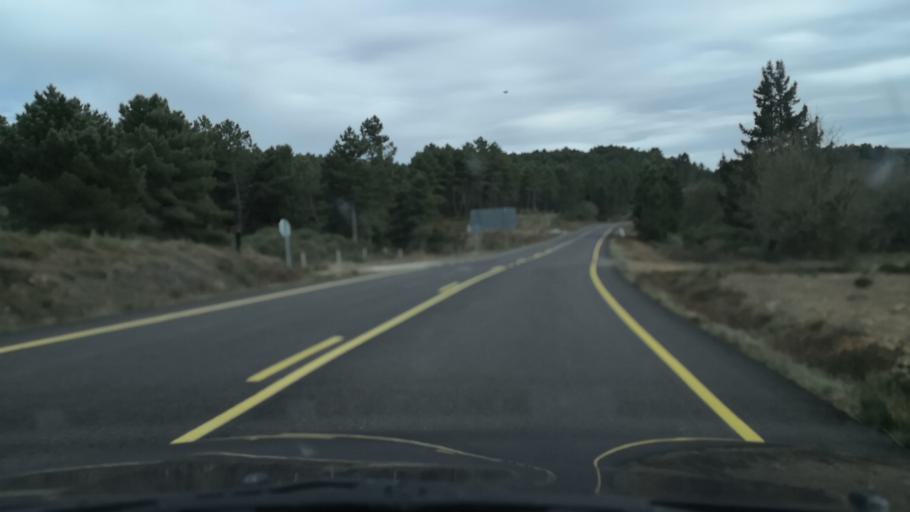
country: ES
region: Extremadura
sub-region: Provincia de Caceres
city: Acebo
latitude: 40.2545
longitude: -6.6884
